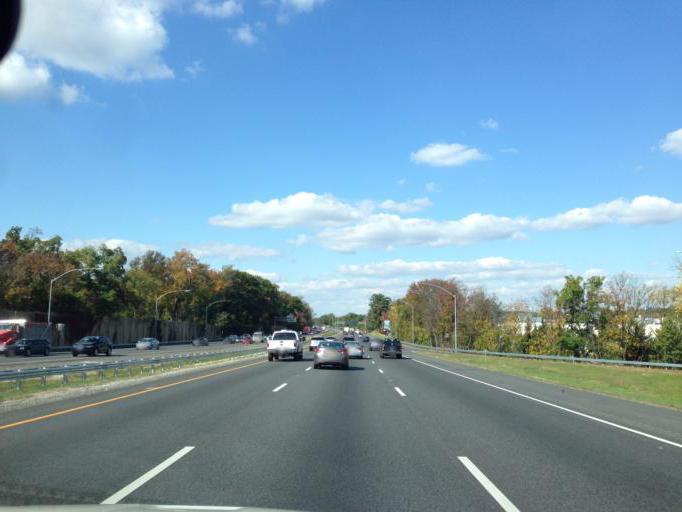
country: US
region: Maryland
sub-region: Baltimore County
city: Timonium
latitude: 39.4397
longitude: -76.6341
